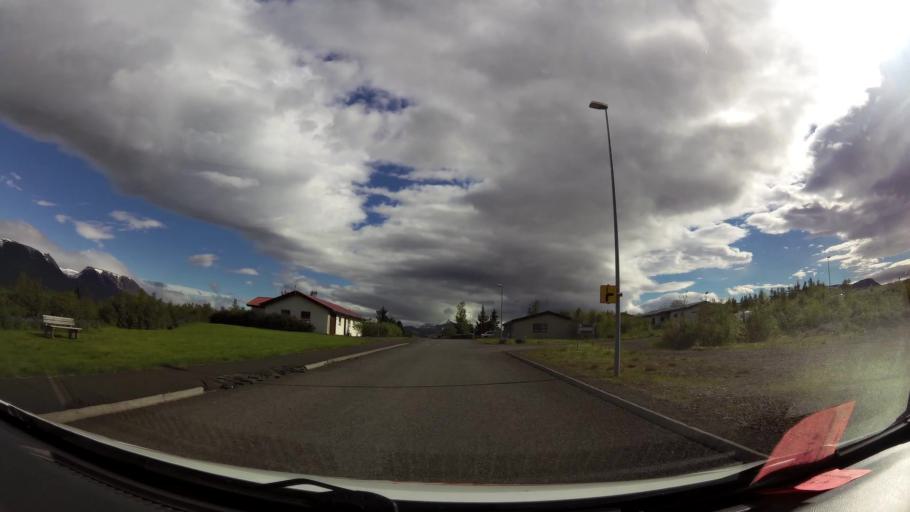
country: IS
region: Northwest
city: Saudarkrokur
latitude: 65.5513
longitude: -19.4488
